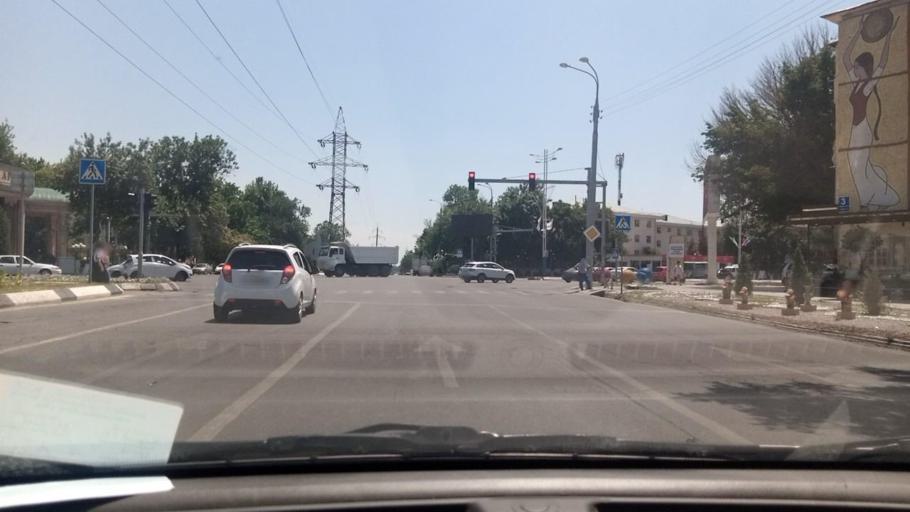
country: UZ
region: Toshkent Shahri
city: Tashkent
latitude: 41.2927
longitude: 69.1940
